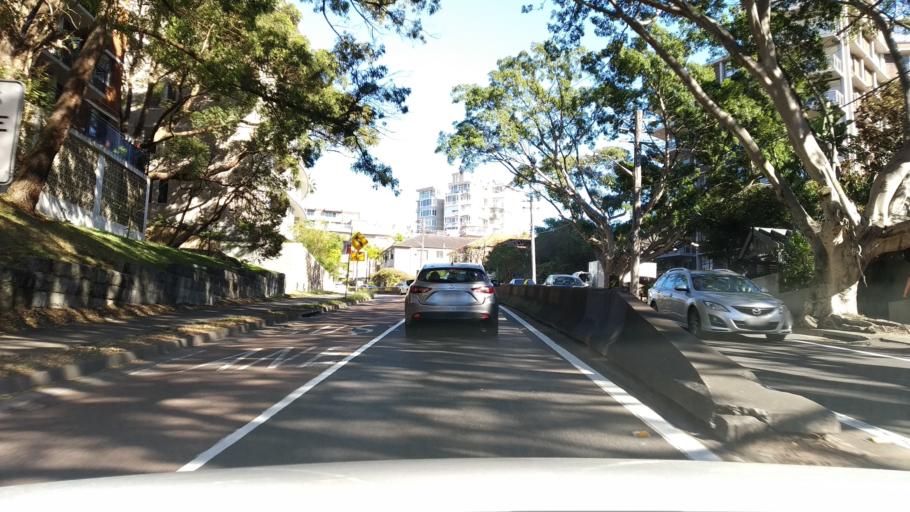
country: AU
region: New South Wales
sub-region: Waverley
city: Bondi
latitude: -33.8883
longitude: 151.2609
